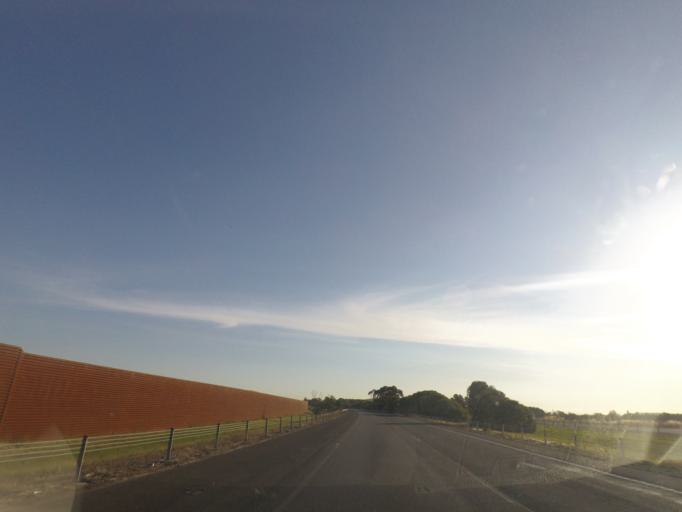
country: AU
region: Victoria
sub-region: Whittlesea
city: Whittlesea
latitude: -37.4290
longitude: 144.9848
